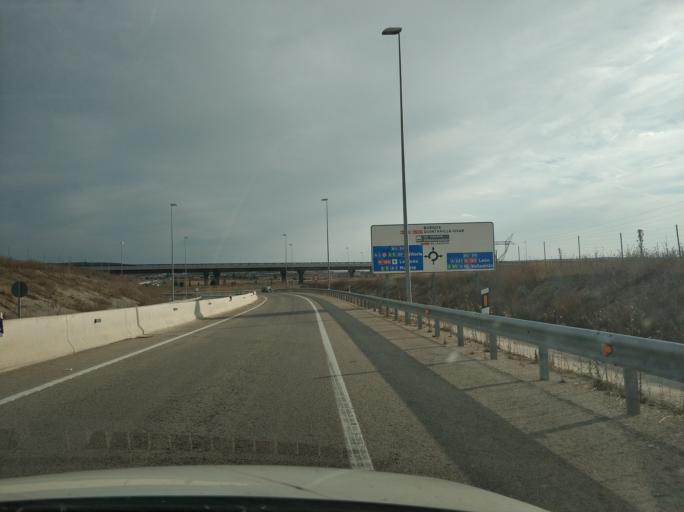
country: ES
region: Castille and Leon
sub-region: Provincia de Burgos
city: Sotragero
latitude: 42.3872
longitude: -3.6955
